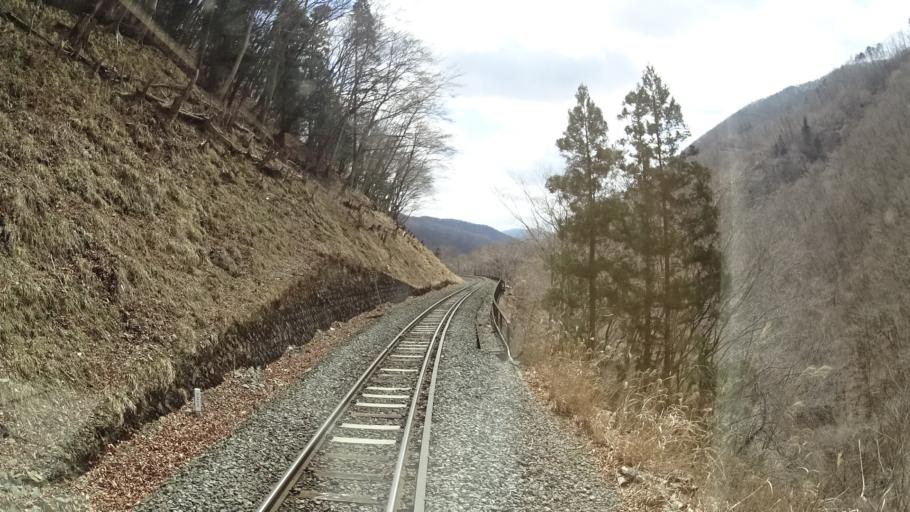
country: JP
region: Iwate
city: Tono
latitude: 39.2420
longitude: 141.6708
